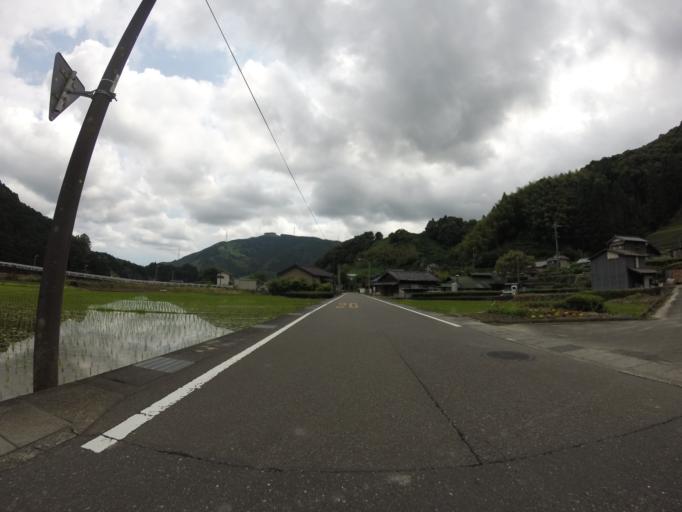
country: JP
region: Shizuoka
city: Shizuoka-shi
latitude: 35.0170
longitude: 138.2814
